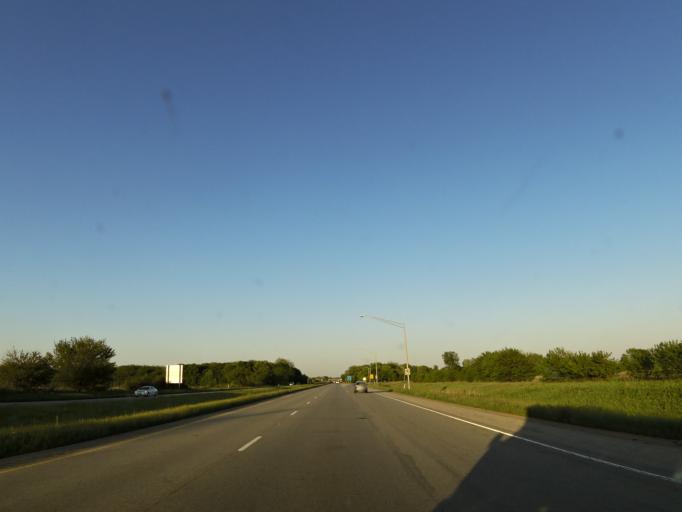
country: US
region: Illinois
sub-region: Vermilion County
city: Danville
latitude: 40.1176
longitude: -87.5116
